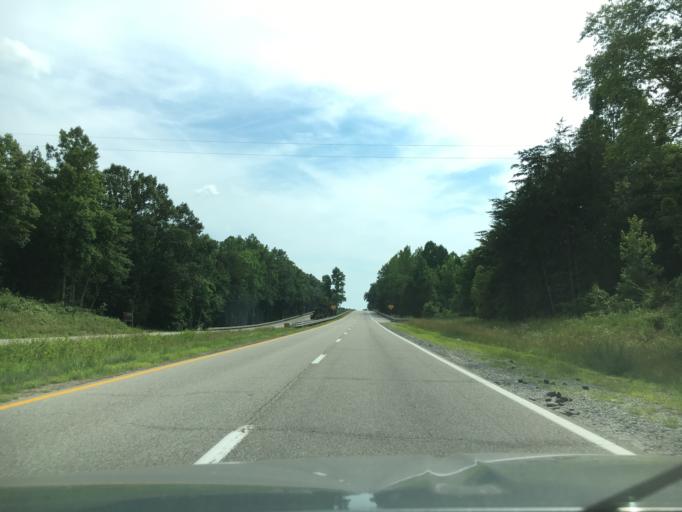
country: US
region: Virginia
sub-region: Prince Edward County
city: Hampden Sydney
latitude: 37.1111
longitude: -78.3516
